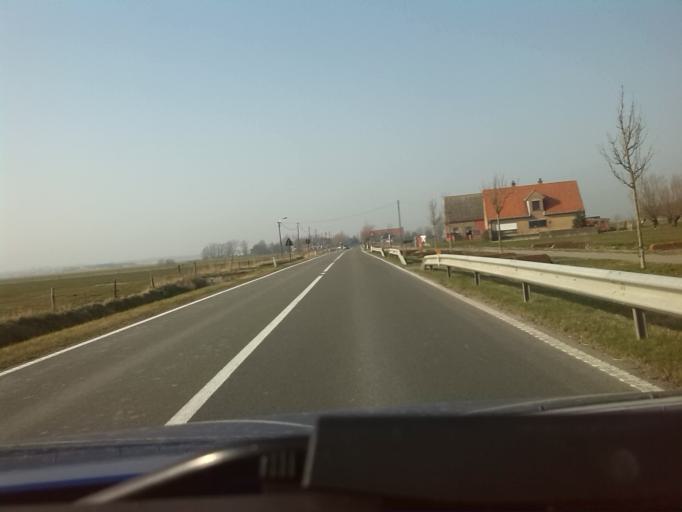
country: BE
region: Flanders
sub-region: Provincie West-Vlaanderen
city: Wenduine
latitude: 51.2703
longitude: 3.0936
